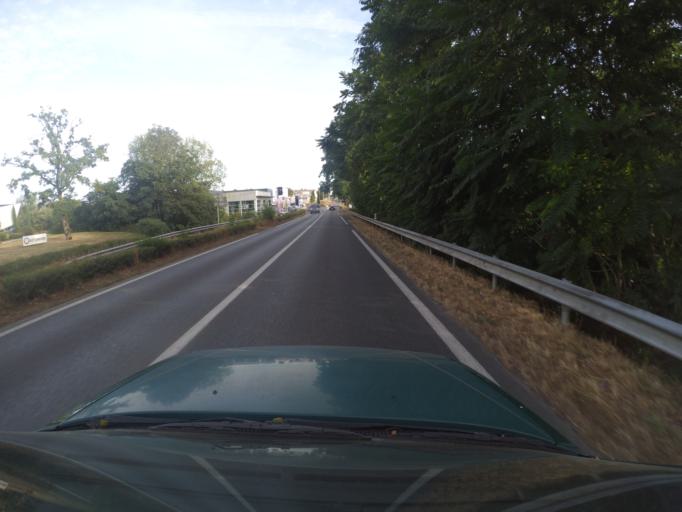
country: FR
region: Pays de la Loire
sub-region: Departement de la Vendee
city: Montaigu
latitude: 46.9855
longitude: -1.3201
